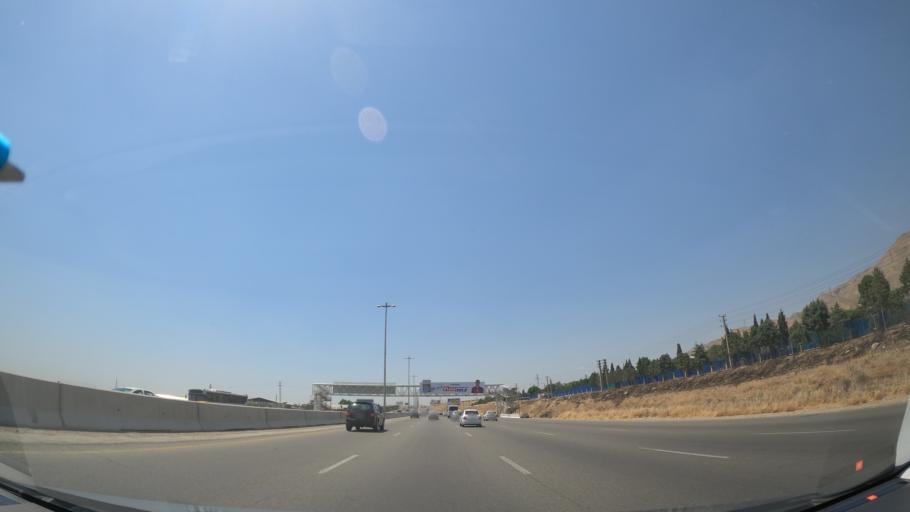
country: IR
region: Tehran
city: Shahr-e Qods
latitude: 35.7632
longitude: 51.0599
